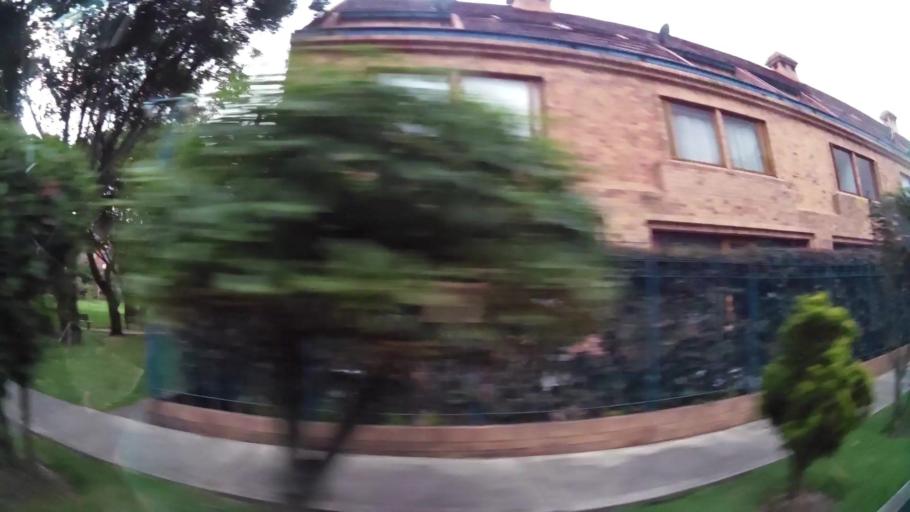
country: CO
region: Bogota D.C.
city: Barrio San Luis
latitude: 4.7246
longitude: -74.0640
